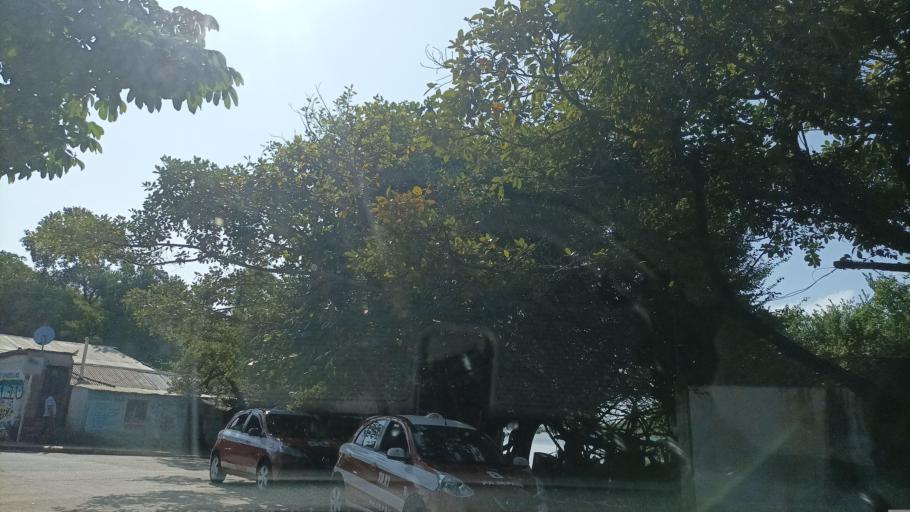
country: MX
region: Veracruz
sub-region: Coatzacoalcos
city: Fraccionamiento Ciudad Olmeca
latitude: 18.2117
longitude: -94.6125
